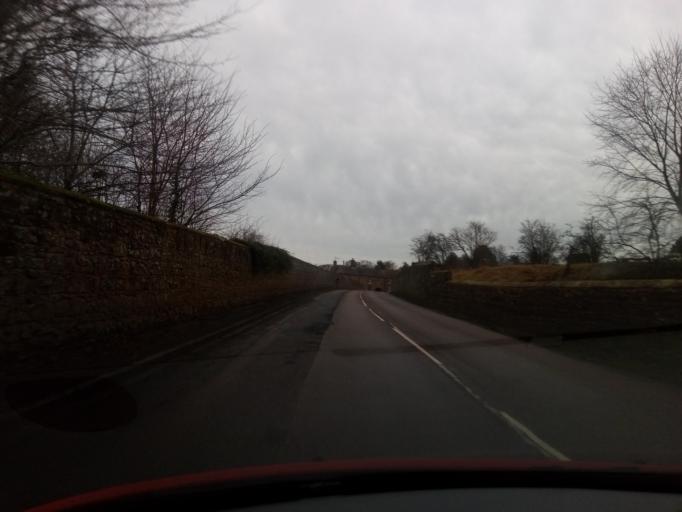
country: GB
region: England
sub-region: Northumberland
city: Alnwick
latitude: 55.4193
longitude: -1.7152
